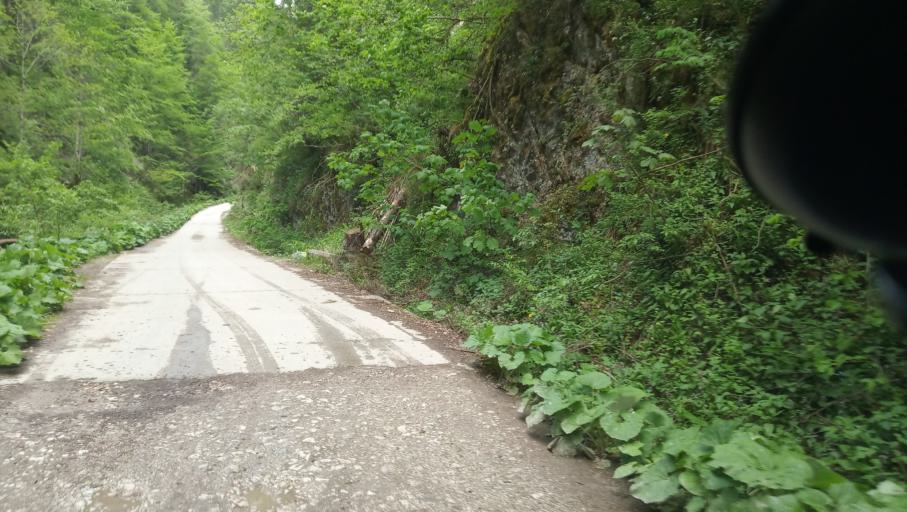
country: RO
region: Alba
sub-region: Comuna Scarisoara
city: Scarisoara
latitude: 46.4692
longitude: 22.8453
